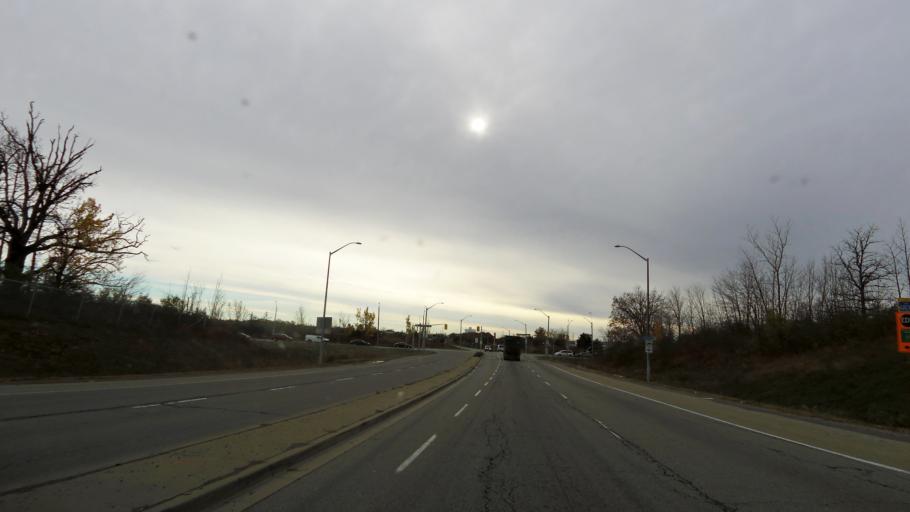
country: CA
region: Ontario
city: Hamilton
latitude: 43.1976
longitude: -79.8285
